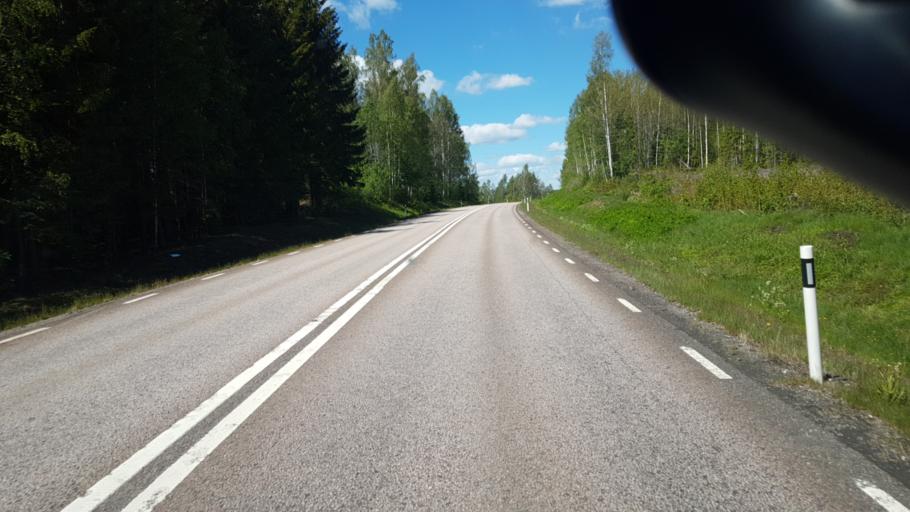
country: SE
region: Vaermland
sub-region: Karlstads Kommun
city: Edsvalla
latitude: 59.5674
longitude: 13.0238
